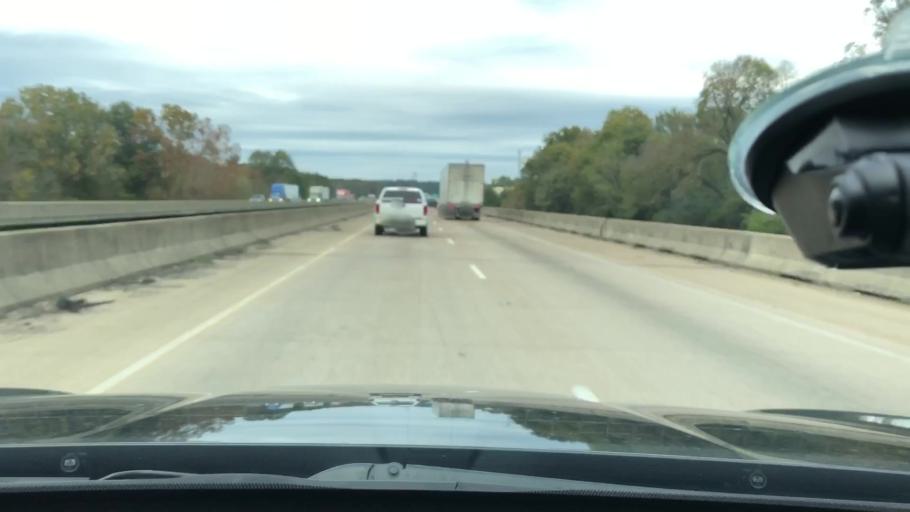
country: US
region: Arkansas
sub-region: Clark County
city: Arkadelphia
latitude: 34.1749
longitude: -93.0742
